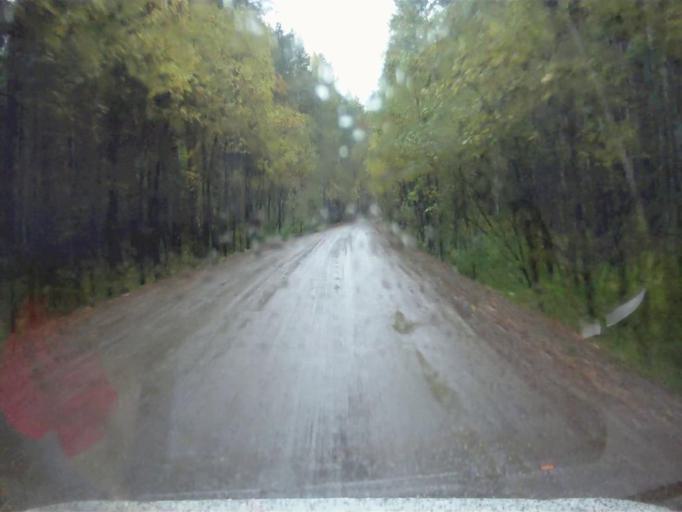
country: RU
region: Chelyabinsk
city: Kyshtym
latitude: 55.8934
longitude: 60.4652
